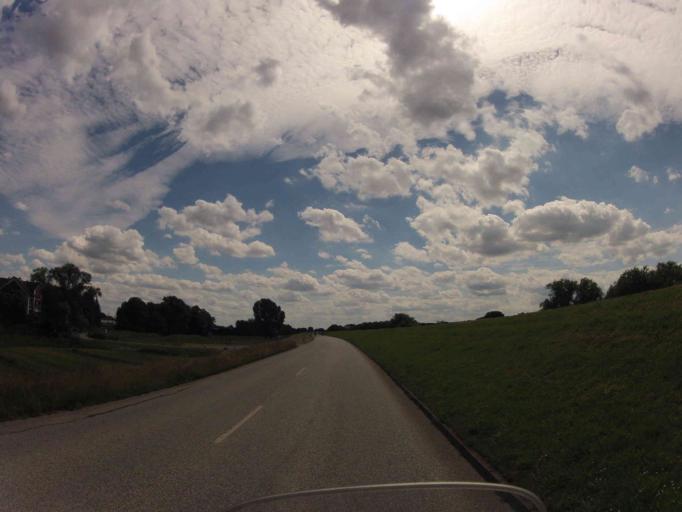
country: DE
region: Hamburg
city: Rothenburgsort
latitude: 53.4946
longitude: 10.0535
